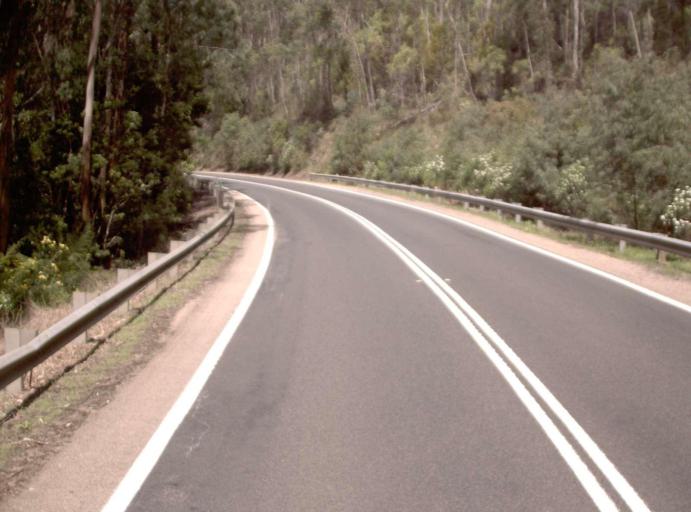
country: AU
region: New South Wales
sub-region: Bombala
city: Bombala
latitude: -37.5360
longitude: 149.3814
